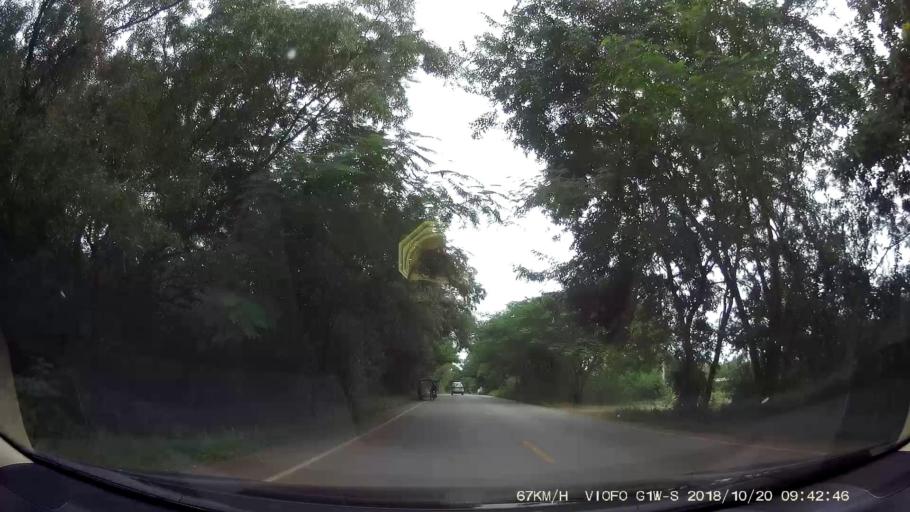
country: TH
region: Chaiyaphum
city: Khon San
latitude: 16.4670
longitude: 101.9510
